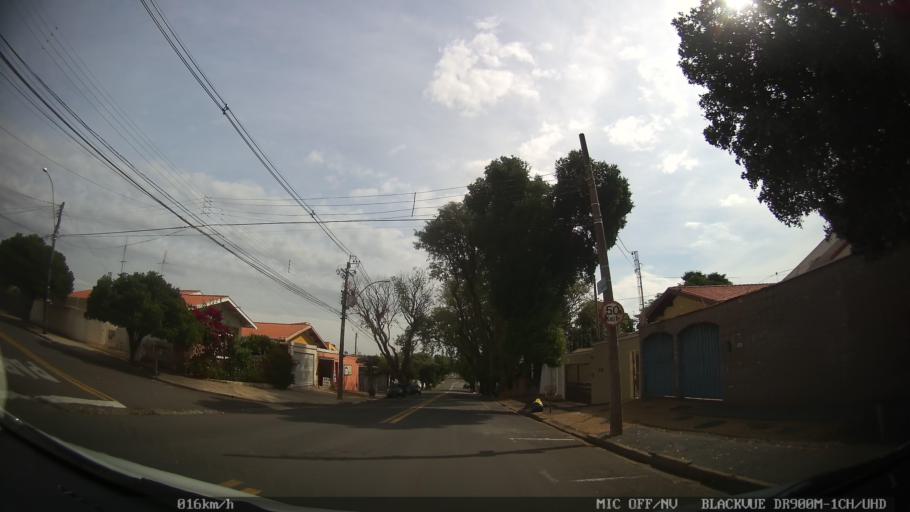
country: BR
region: Sao Paulo
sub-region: Piracicaba
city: Piracicaba
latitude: -22.7160
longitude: -47.6642
